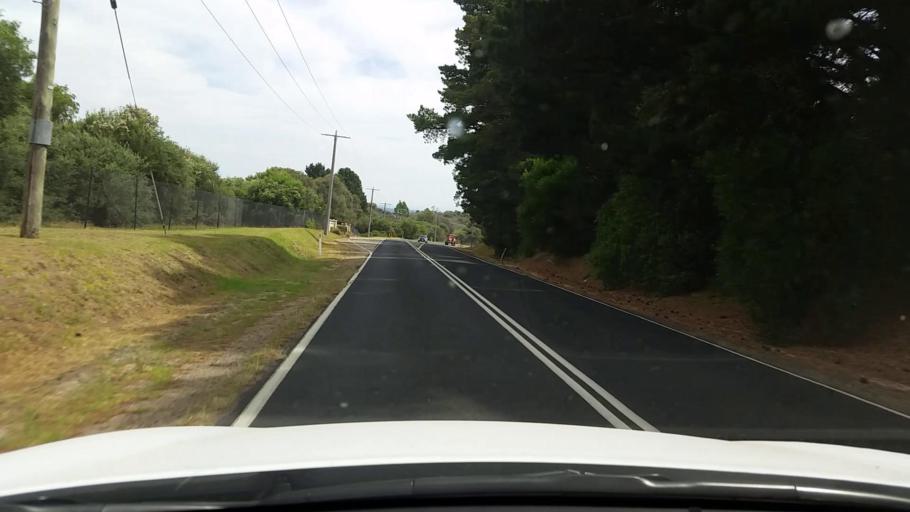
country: AU
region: Victoria
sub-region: Mornington Peninsula
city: Saint Andrews Beach
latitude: -38.4568
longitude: 144.9006
